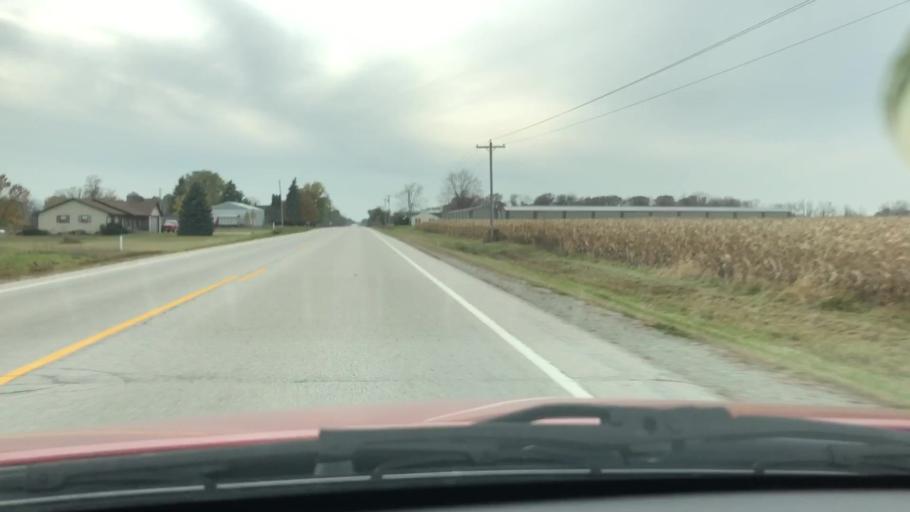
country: US
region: Wisconsin
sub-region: Brown County
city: Oneida
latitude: 44.4443
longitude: -88.1523
